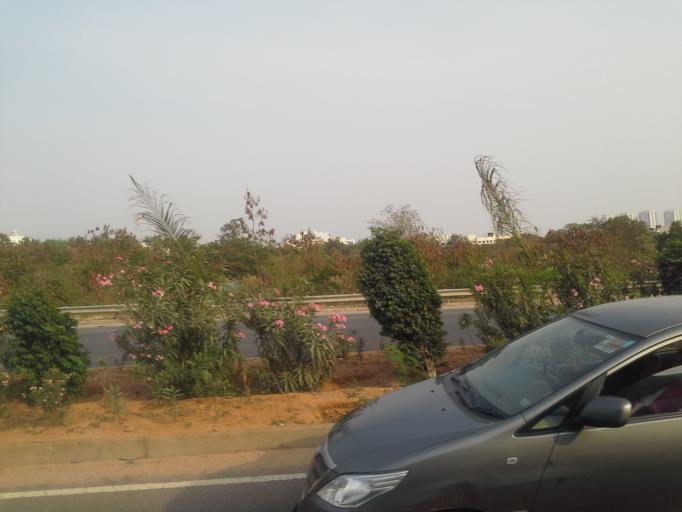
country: IN
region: Telangana
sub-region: Rangareddi
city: Kukatpalli
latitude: 17.4262
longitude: 78.3581
